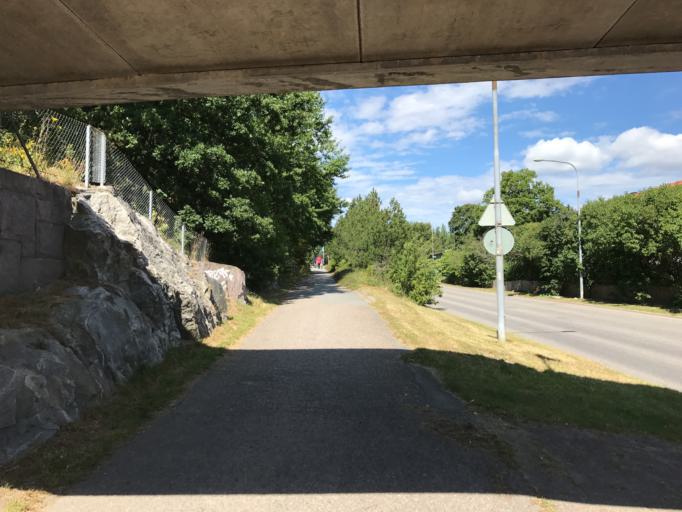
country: SE
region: Stockholm
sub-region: Stockholms Kommun
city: Kista
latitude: 59.4025
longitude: 17.9330
